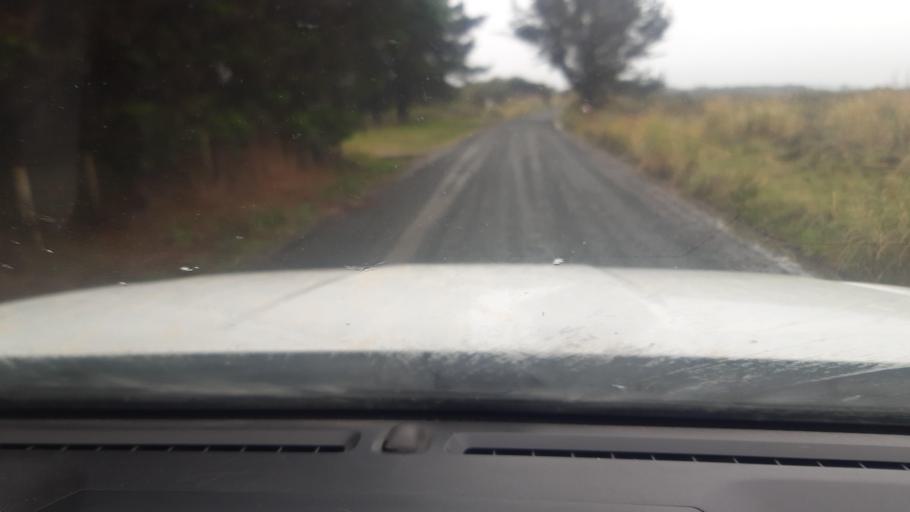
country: NZ
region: Northland
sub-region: Far North District
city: Kaitaia
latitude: -34.9108
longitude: 173.2692
